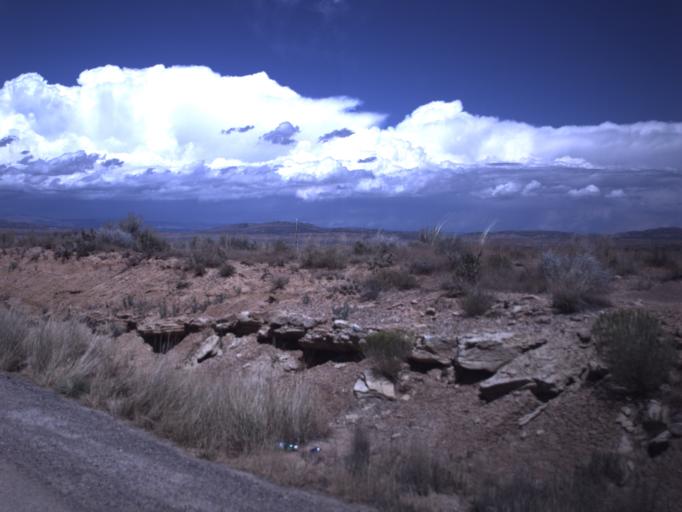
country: US
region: Utah
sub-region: Uintah County
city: Maeser
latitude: 40.2905
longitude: -109.6852
